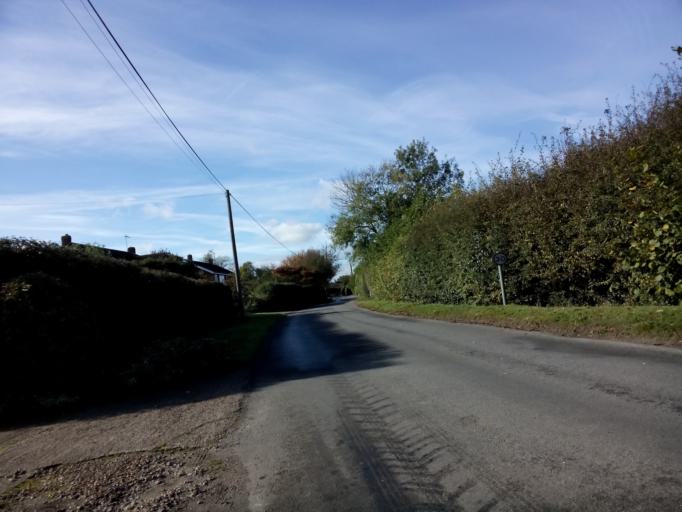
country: GB
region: England
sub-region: Suffolk
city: Capel Saint Mary
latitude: 52.0385
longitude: 1.0468
